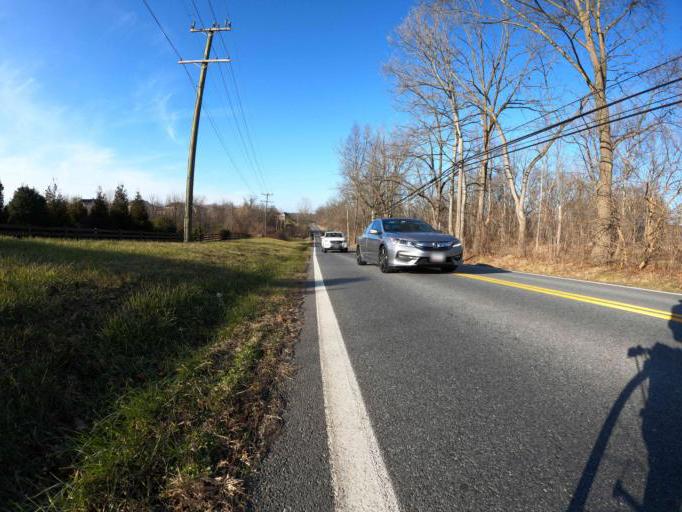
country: US
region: Maryland
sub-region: Howard County
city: Highland
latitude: 39.2354
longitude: -76.9400
